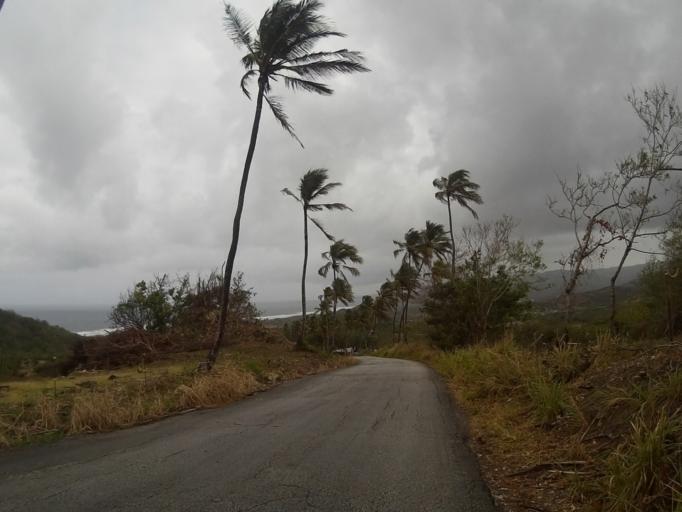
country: BB
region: Saint Andrew
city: Greenland
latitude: 13.2703
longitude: -59.5766
